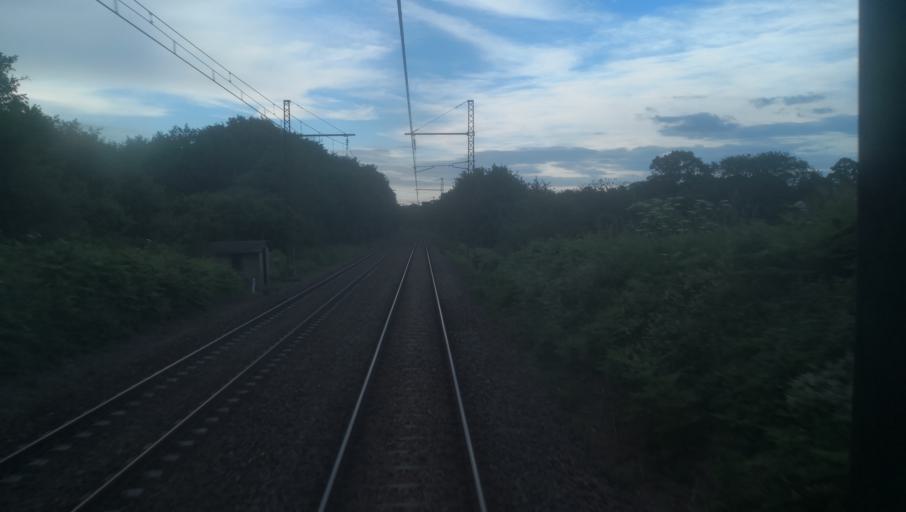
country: FR
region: Limousin
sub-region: Departement de la Creuse
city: La Souterraine
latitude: 46.2098
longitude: 1.4803
